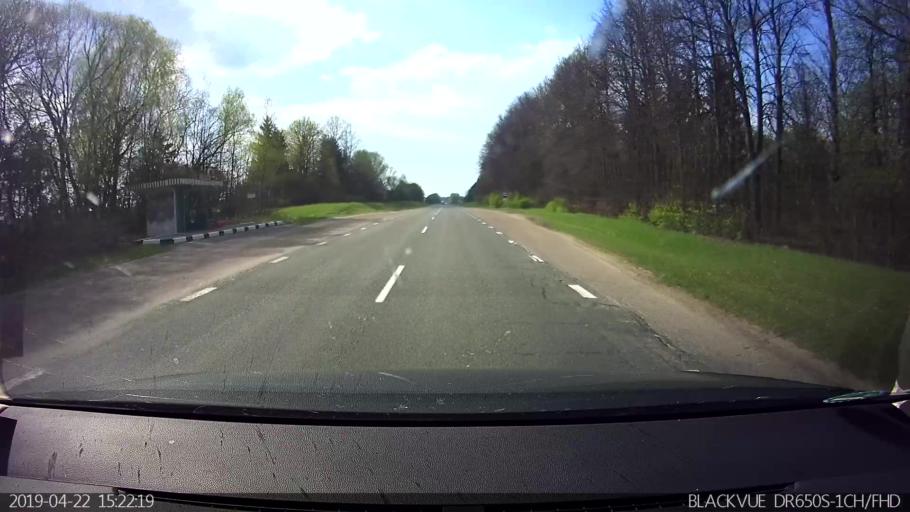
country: BY
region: Brest
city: Vysokaye
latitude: 52.3492
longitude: 23.4489
